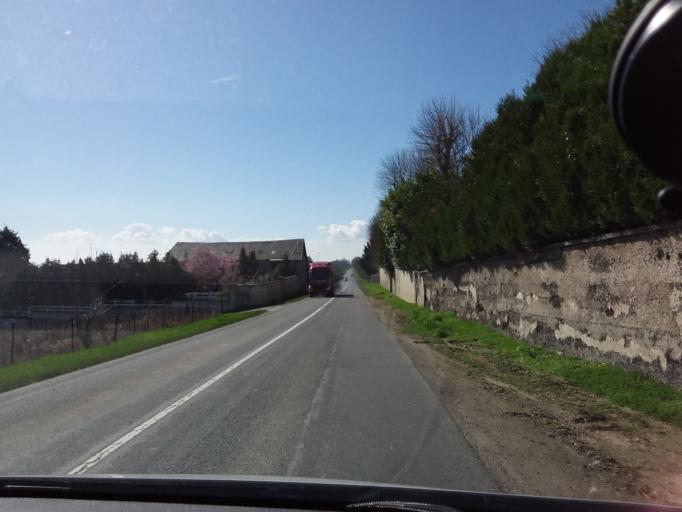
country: FR
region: Picardie
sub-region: Departement de l'Aisne
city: Guignicourt
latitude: 49.4428
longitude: 4.0381
